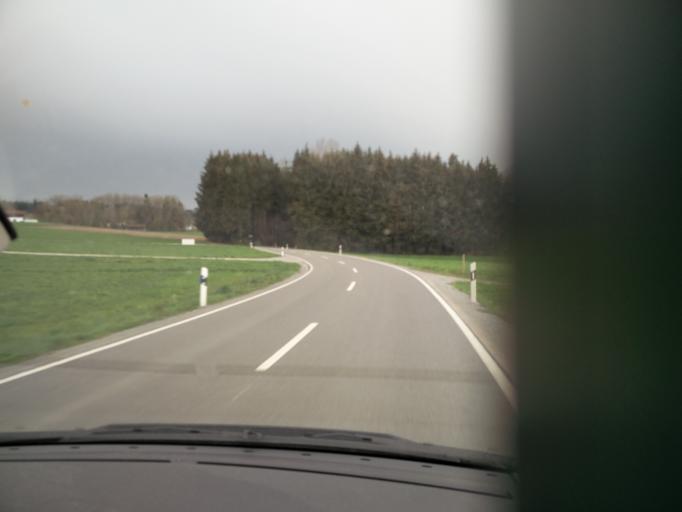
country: DE
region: Bavaria
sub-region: Upper Bavaria
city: Halfing
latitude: 47.9668
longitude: 12.2935
